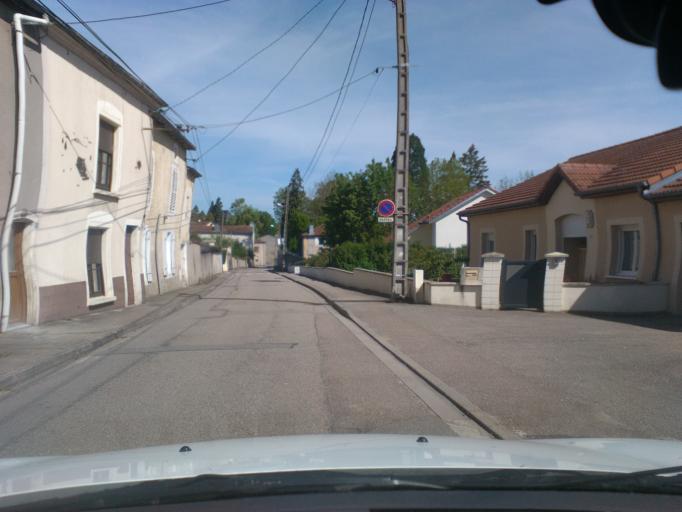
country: FR
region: Lorraine
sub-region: Departement des Vosges
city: Mirecourt
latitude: 48.2974
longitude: 6.1360
